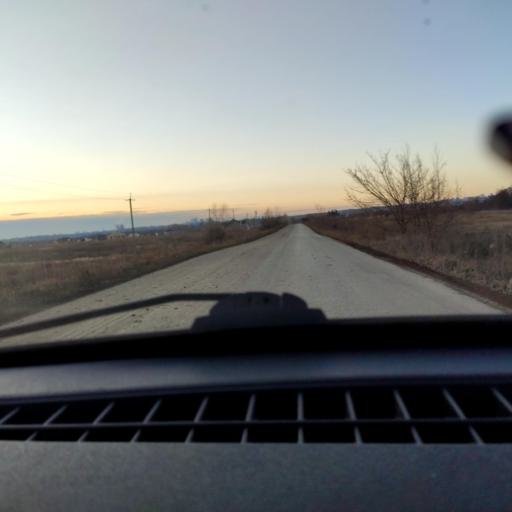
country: RU
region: Bashkortostan
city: Ufa
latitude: 54.7037
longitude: 56.1165
